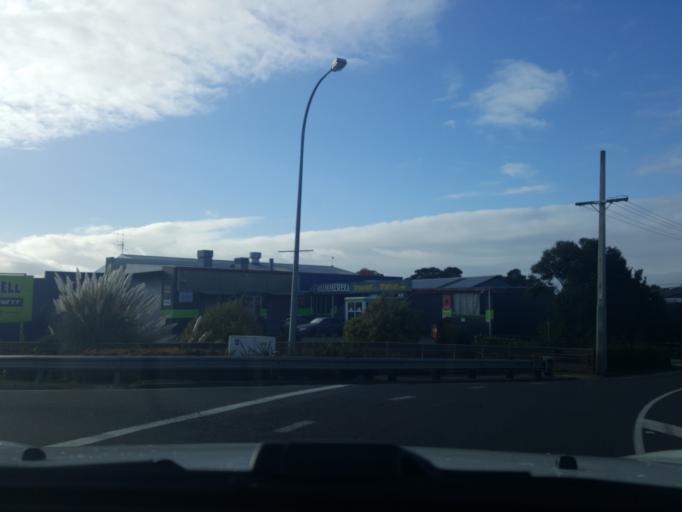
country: NZ
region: Waikato
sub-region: Waipa District
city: Cambridge
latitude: -37.6594
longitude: 175.5245
